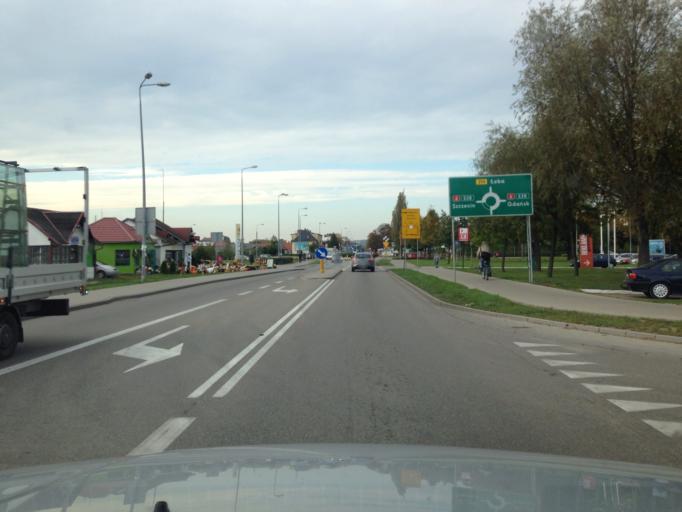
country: PL
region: Pomeranian Voivodeship
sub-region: Powiat leborski
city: Lebork
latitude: 54.5317
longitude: 17.7602
